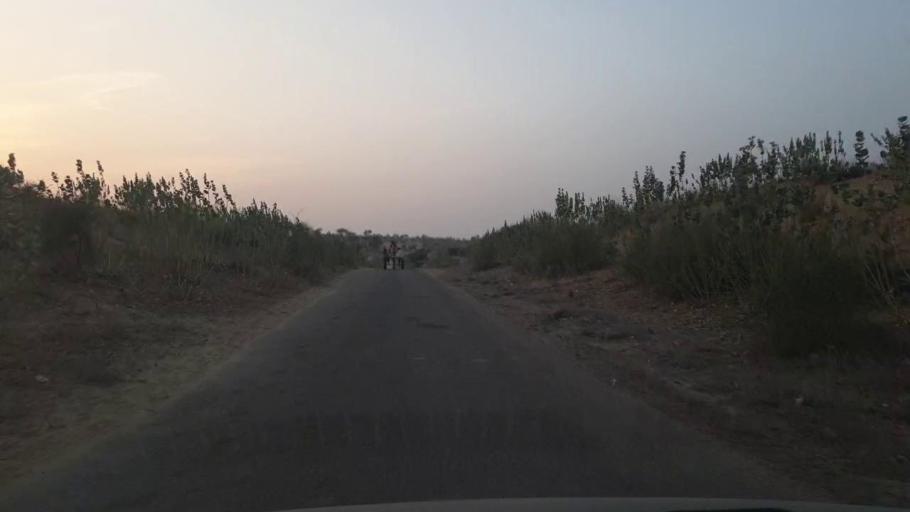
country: PK
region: Sindh
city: Umarkot
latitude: 25.3098
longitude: 70.0650
